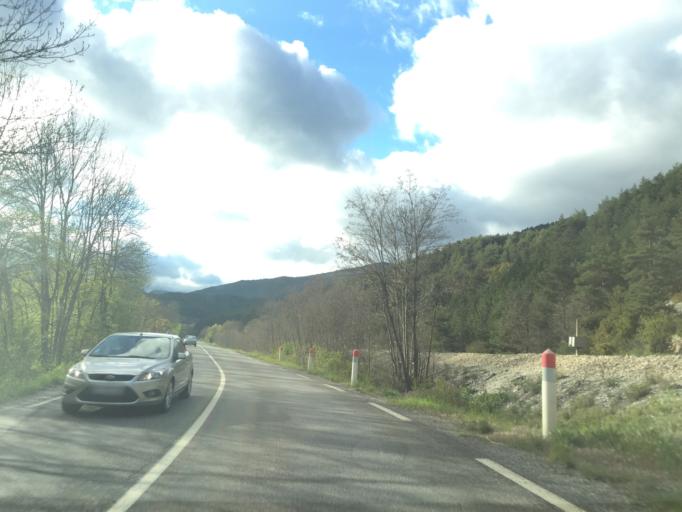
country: FR
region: Provence-Alpes-Cote d'Azur
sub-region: Departement des Hautes-Alpes
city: Veynes
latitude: 44.5607
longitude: 5.7653
